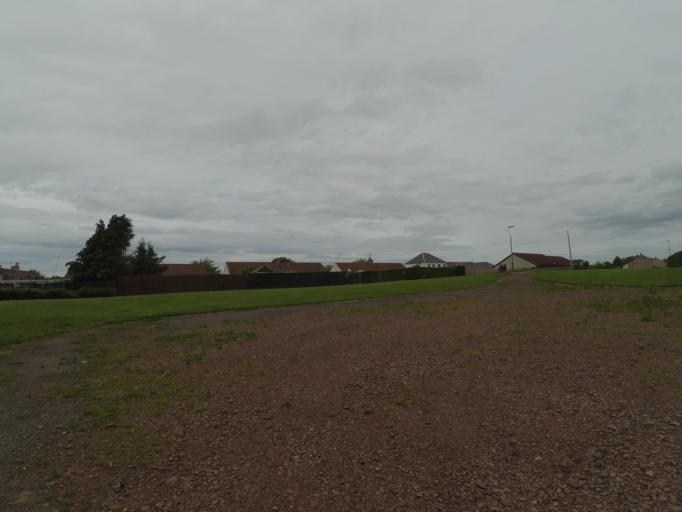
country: GB
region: Scotland
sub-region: East Lothian
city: Macmerry
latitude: 55.9407
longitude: -2.9067
